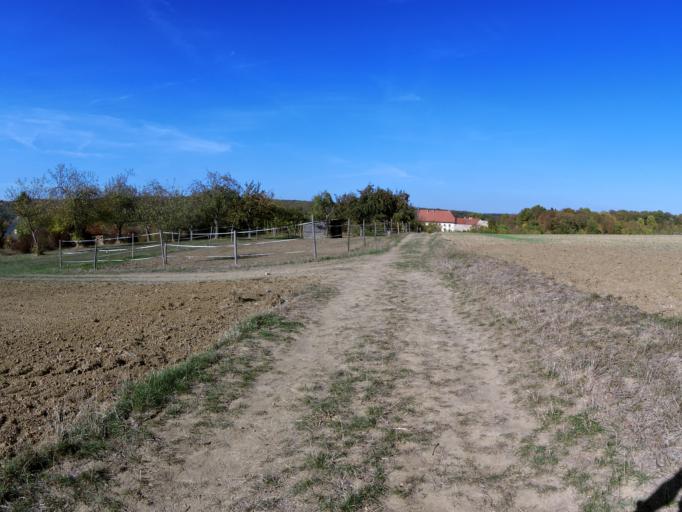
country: DE
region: Bavaria
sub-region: Regierungsbezirk Unterfranken
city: Reichenberg
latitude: 49.7285
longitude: 9.9197
